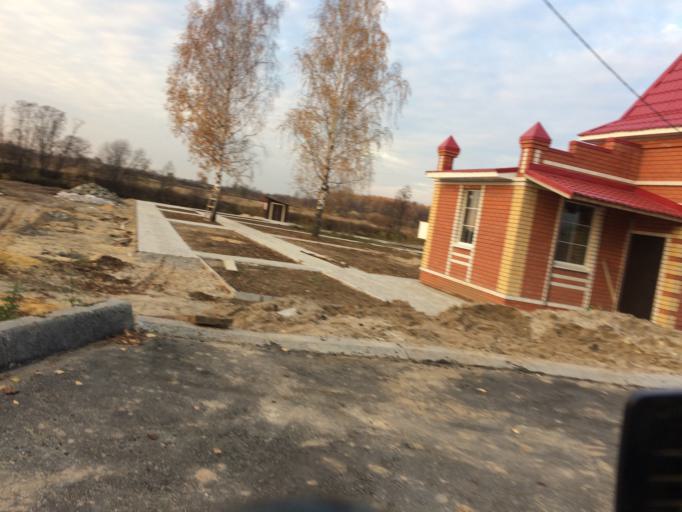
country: RU
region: Mariy-El
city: Yoshkar-Ola
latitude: 56.6442
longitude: 47.9258
